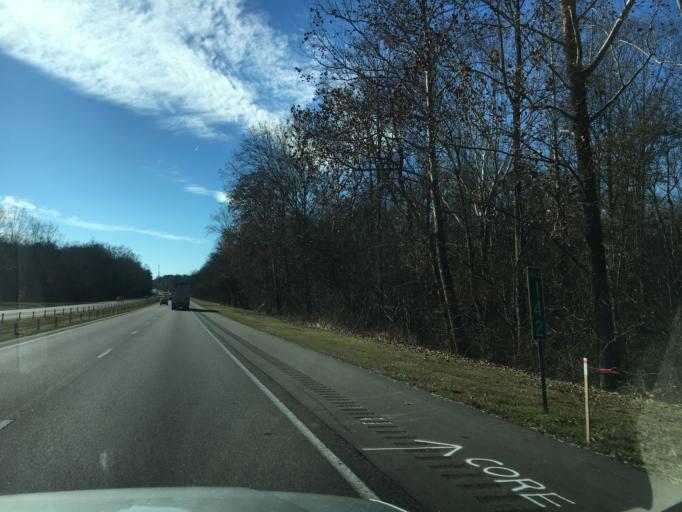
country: US
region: North Carolina
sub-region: Alexander County
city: Stony Point
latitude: 35.7601
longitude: -81.0331
